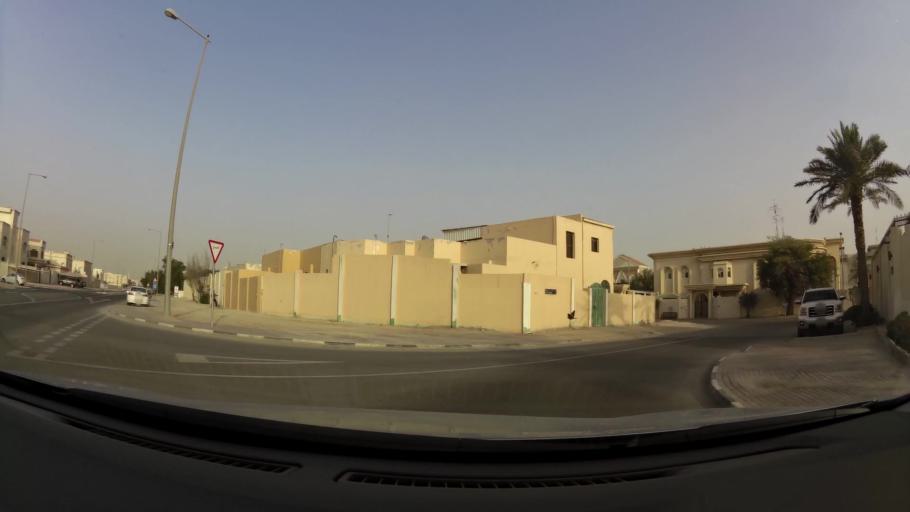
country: QA
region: Baladiyat ar Rayyan
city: Ar Rayyan
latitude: 25.2506
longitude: 51.4472
